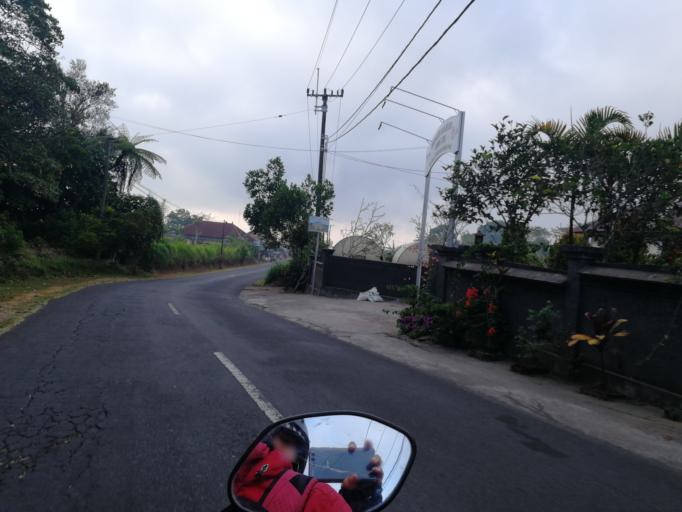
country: ID
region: Bali
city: Banjar Ambengan
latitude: -8.2258
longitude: 115.2448
